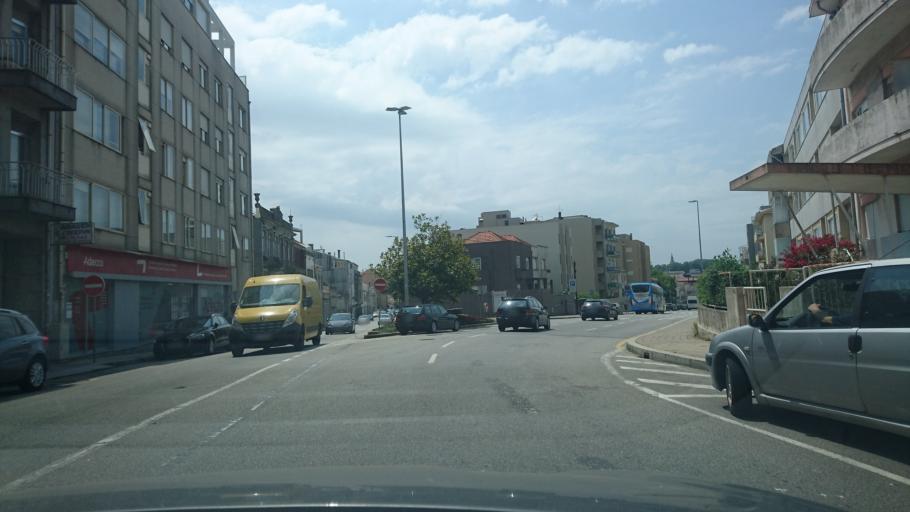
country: PT
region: Porto
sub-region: Porto
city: Porto
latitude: 41.1606
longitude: -8.5935
